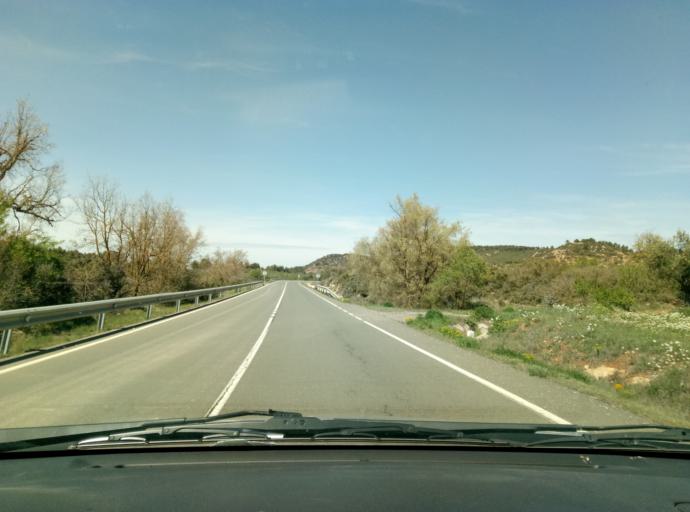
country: ES
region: Catalonia
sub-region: Provincia de Lleida
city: Vinaixa
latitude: 41.4245
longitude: 0.9113
